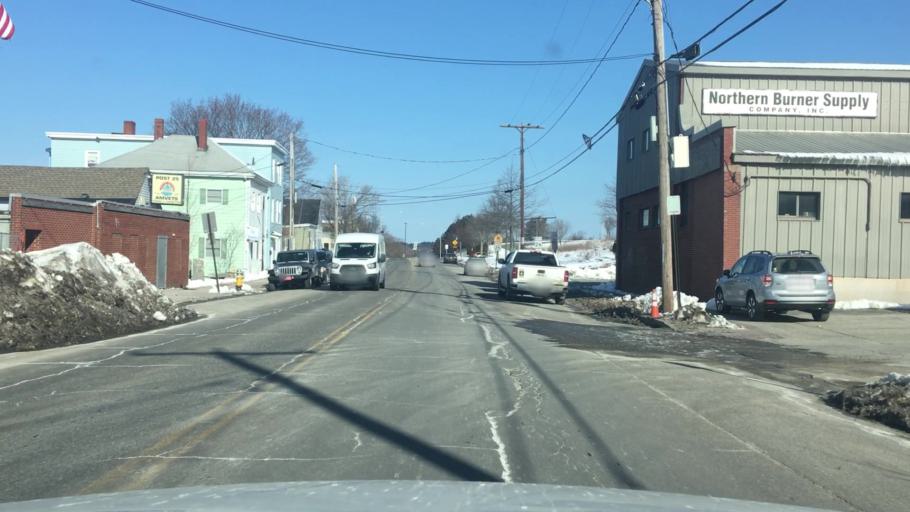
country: US
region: Maine
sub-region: Cumberland County
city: Portland
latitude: 43.6691
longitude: -70.2542
